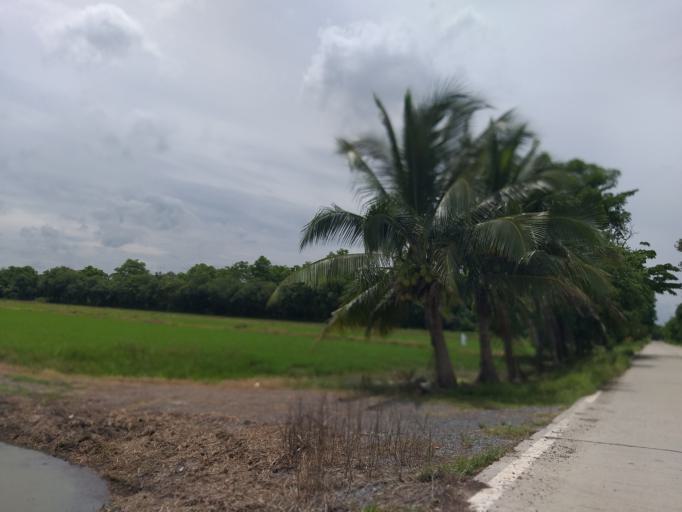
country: TH
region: Pathum Thani
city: Ban Lam Luk Ka
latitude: 14.0310
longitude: 100.8660
